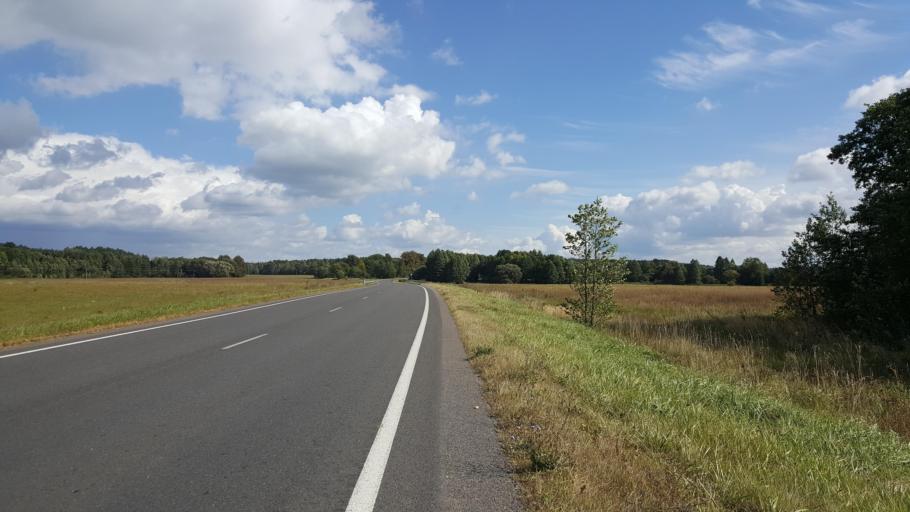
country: BY
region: Brest
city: Kamyanyets
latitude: 52.3996
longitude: 23.8903
